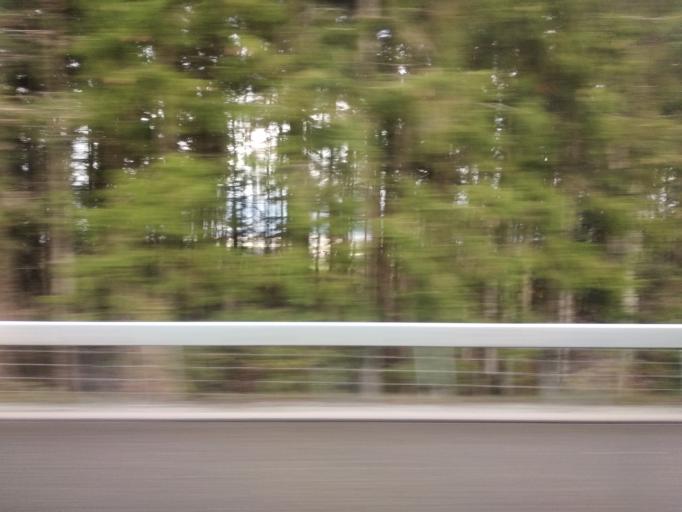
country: CH
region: Thurgau
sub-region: Frauenfeld District
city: Gachnang
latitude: 47.5303
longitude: 8.8589
